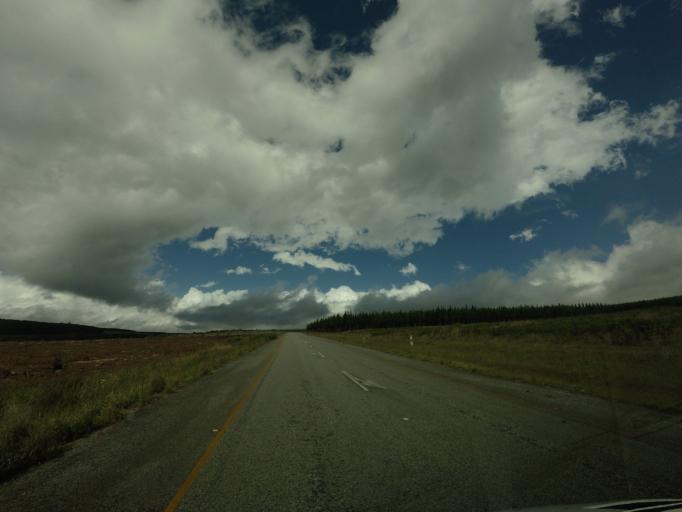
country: ZA
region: Mpumalanga
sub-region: Ehlanzeni District
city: Graksop
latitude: -24.8650
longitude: 30.8528
